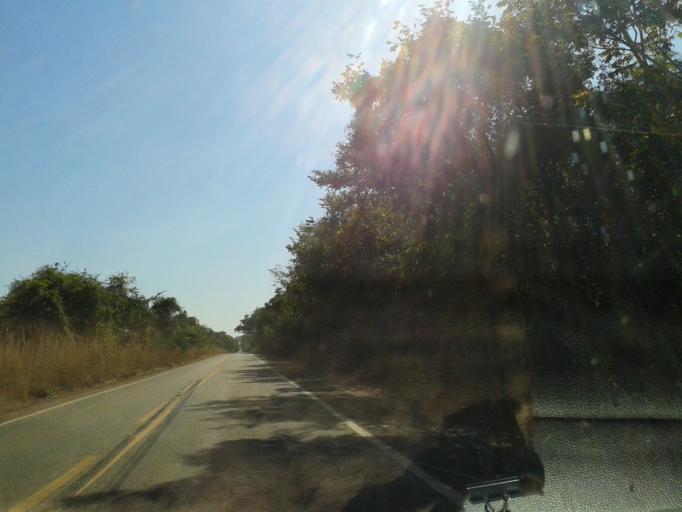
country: BR
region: Goias
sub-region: Mozarlandia
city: Mozarlandia
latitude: -14.4217
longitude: -50.4510
